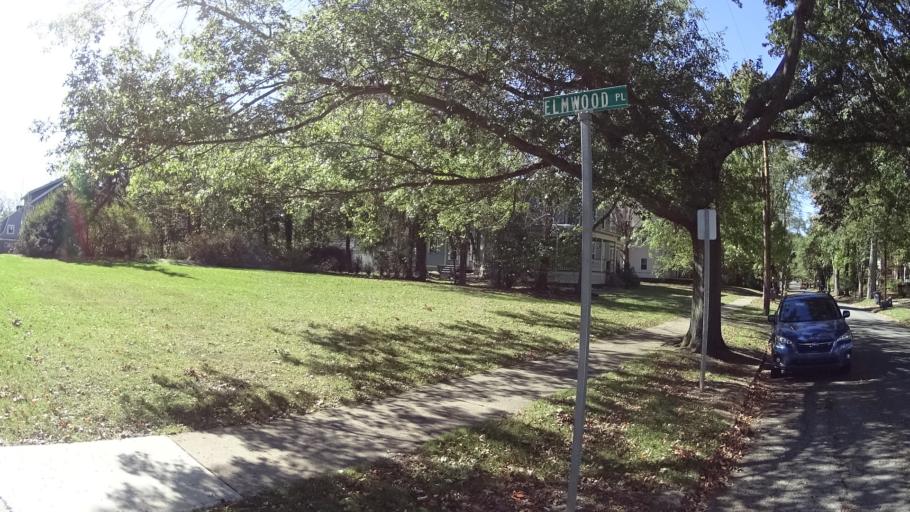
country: US
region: Ohio
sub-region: Lorain County
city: Oberlin
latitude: 41.2904
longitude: -82.2225
